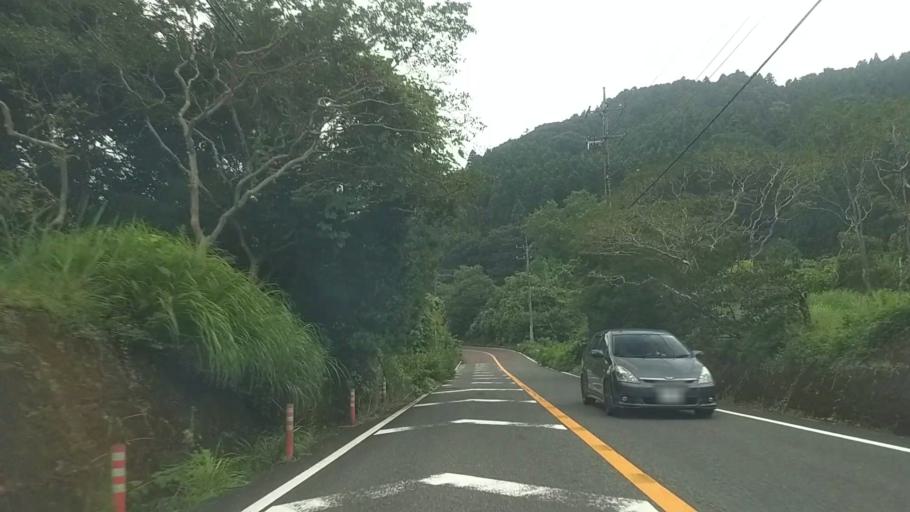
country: JP
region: Chiba
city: Kawaguchi
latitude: 35.2239
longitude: 140.0719
